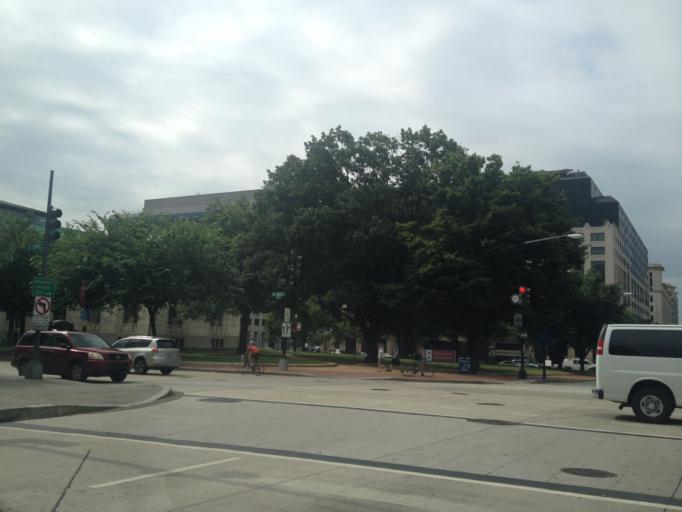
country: US
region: Washington, D.C.
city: Washington, D.C.
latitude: 38.9032
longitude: -77.0240
